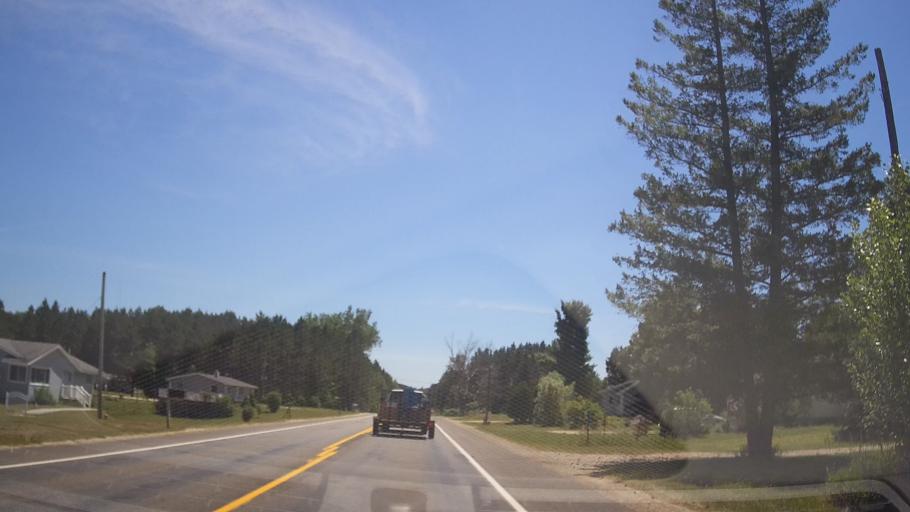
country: US
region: Michigan
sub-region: Grand Traverse County
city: Traverse City
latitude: 44.6504
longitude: -85.6965
